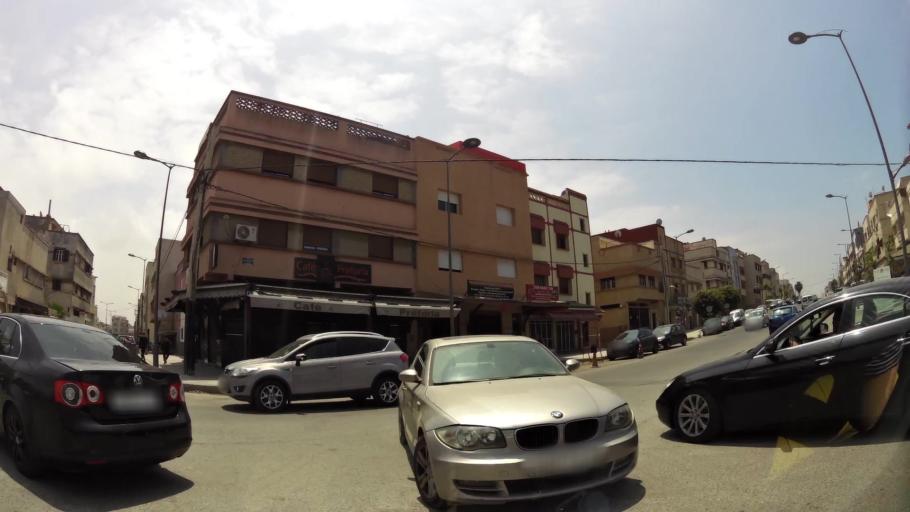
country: MA
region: Rabat-Sale-Zemmour-Zaer
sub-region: Skhirate-Temara
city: Temara
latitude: 33.9816
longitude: -6.8870
